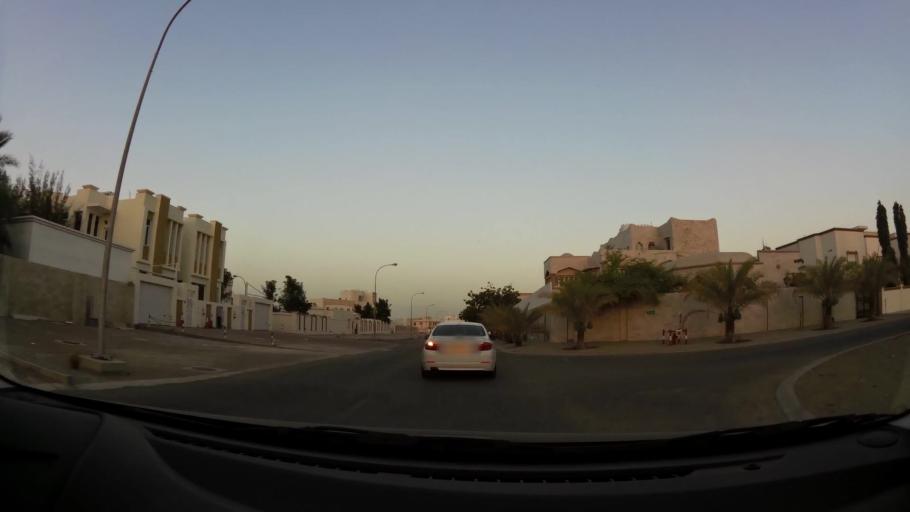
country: OM
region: Muhafazat Masqat
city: As Sib al Jadidah
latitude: 23.6470
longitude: 58.2110
